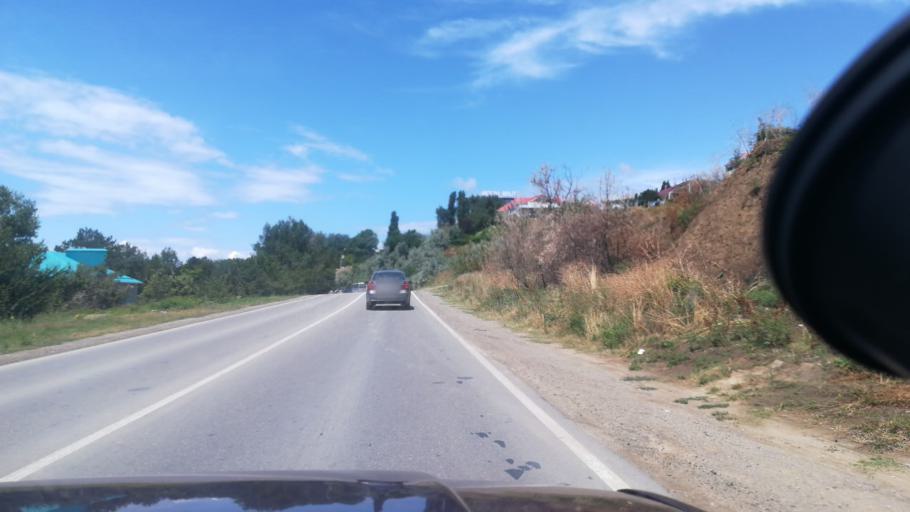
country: RU
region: Krasnodarskiy
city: Vityazevo
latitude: 44.9740
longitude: 37.2776
